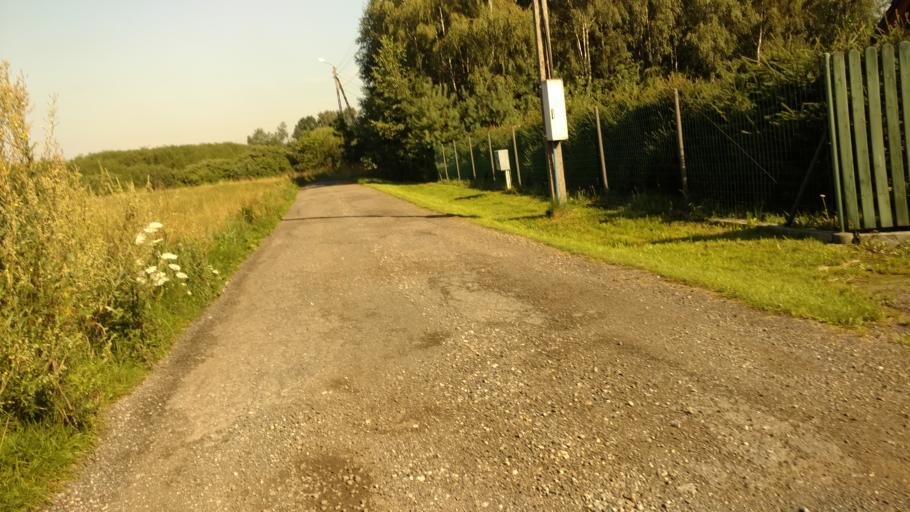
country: PL
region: Silesian Voivodeship
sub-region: Powiat pszczynski
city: Jankowice
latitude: 49.9848
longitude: 18.9905
